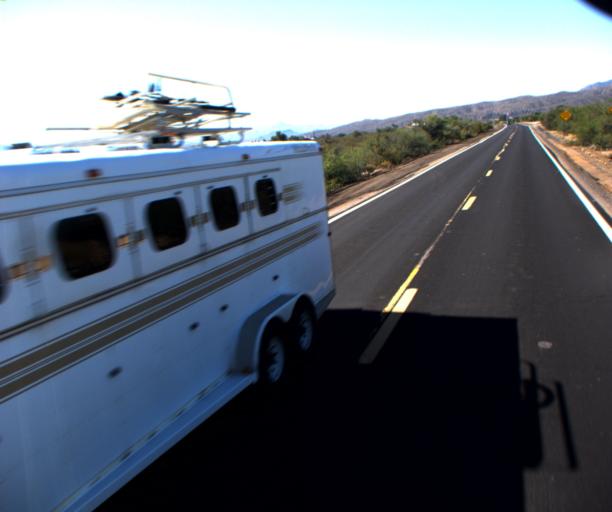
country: US
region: Arizona
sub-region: Yavapai County
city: Bagdad
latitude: 34.7228
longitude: -113.6150
